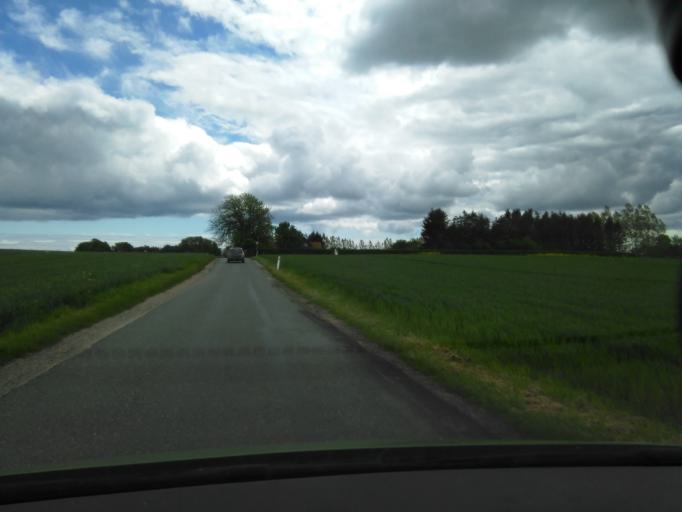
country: DK
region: Central Jutland
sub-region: Arhus Kommune
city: Marslet
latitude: 56.0543
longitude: 10.1314
